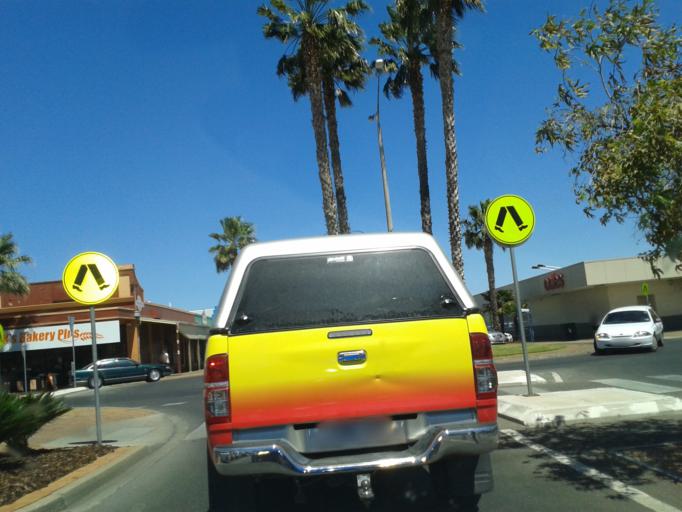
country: AU
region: Victoria
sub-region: Mildura Shire
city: Mildura
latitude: -34.1831
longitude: 142.1607
